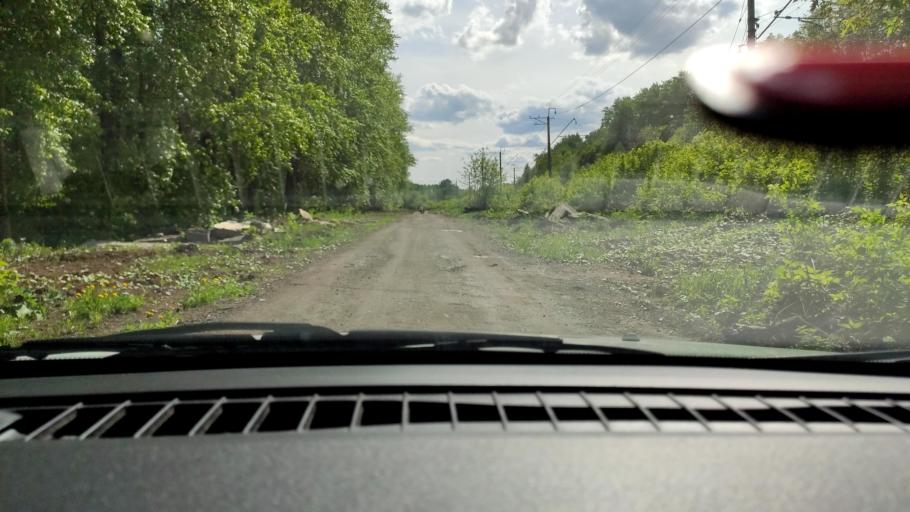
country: RU
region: Perm
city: Perm
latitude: 57.9665
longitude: 56.2072
